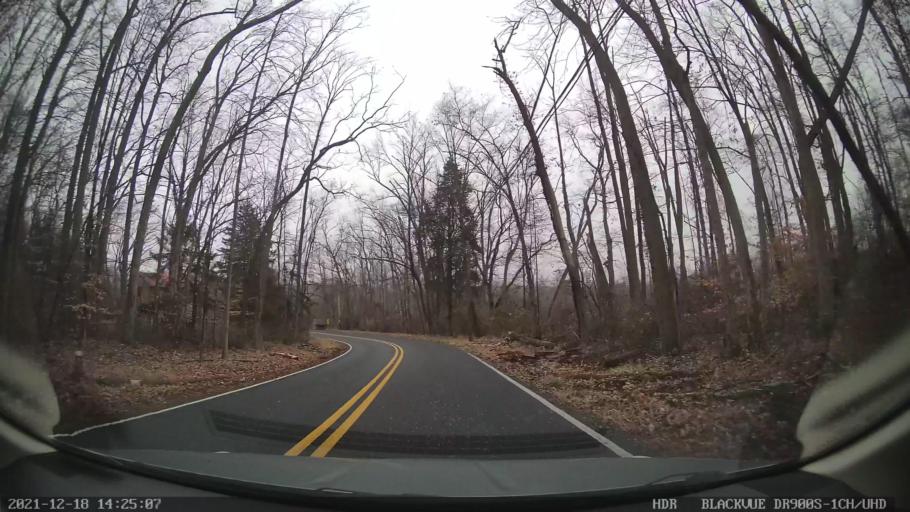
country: US
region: Pennsylvania
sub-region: Berks County
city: Oley
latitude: 40.4160
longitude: -75.7454
